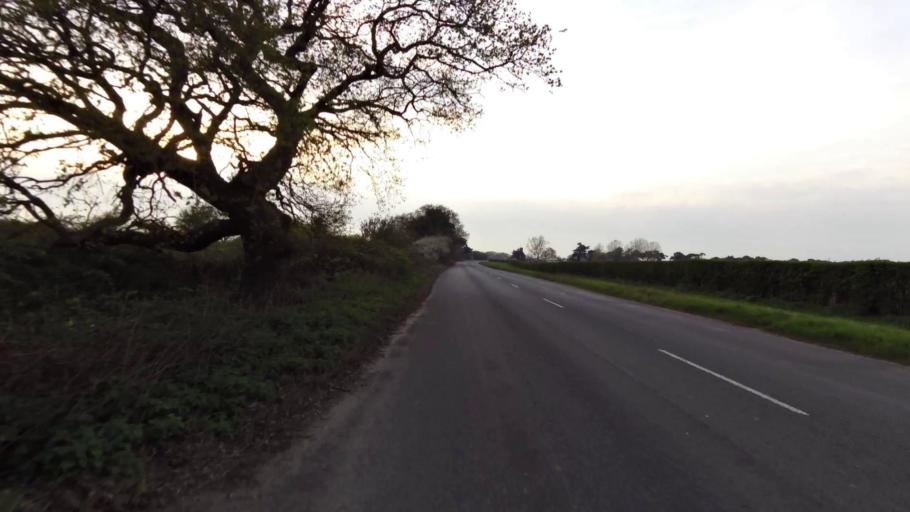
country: GB
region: England
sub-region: Suffolk
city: Shotley Gate
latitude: 52.0091
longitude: 1.2758
